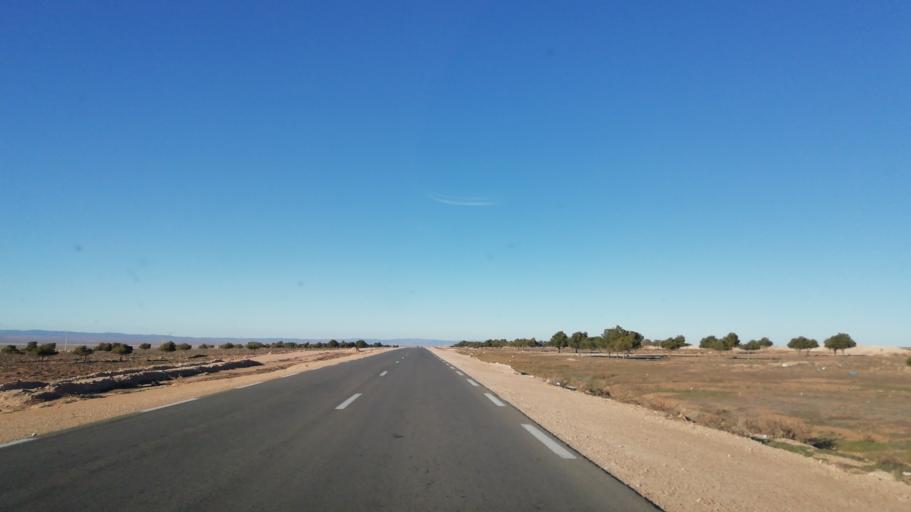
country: DZ
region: Tlemcen
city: Sebdou
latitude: 34.2824
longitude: -1.2593
